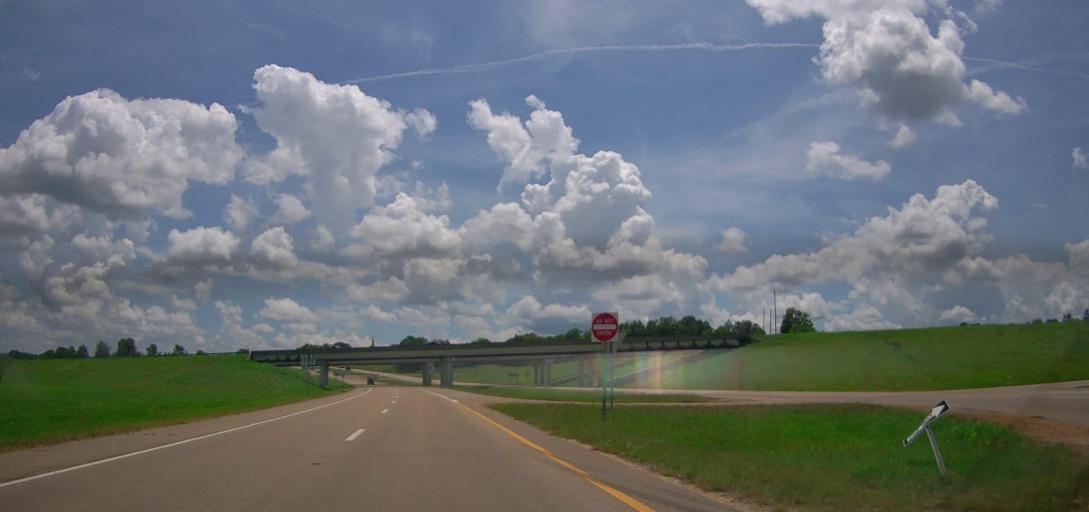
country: US
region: Mississippi
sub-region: Lee County
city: Tupelo
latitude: 34.3155
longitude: -88.7896
